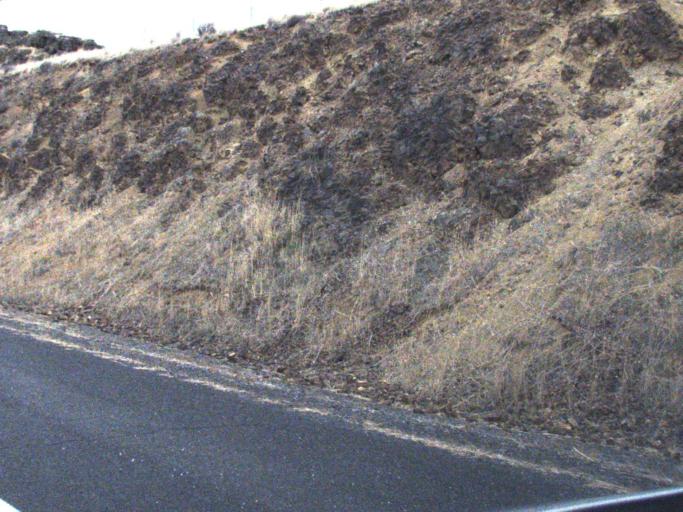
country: US
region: Washington
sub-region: Adams County
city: Ritzville
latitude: 46.7696
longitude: -118.1229
